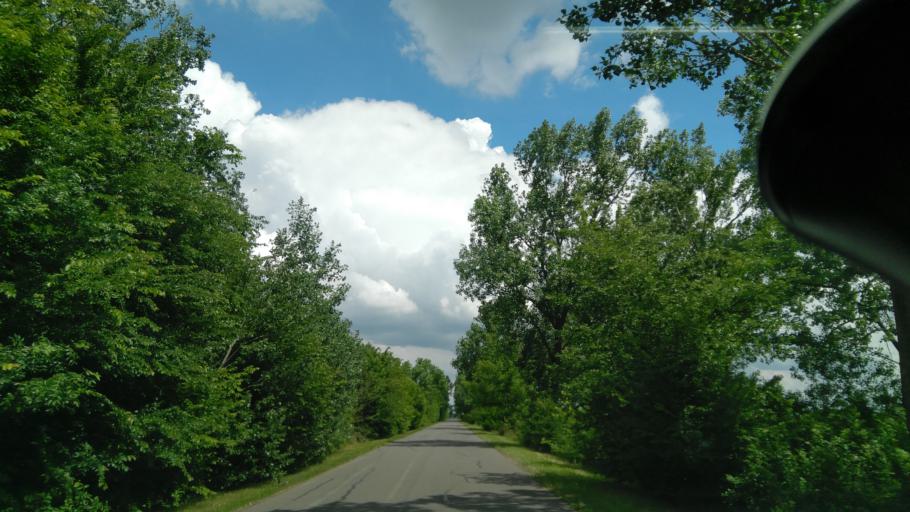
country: HU
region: Bekes
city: Gyomaendrod
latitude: 46.9850
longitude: 20.8929
